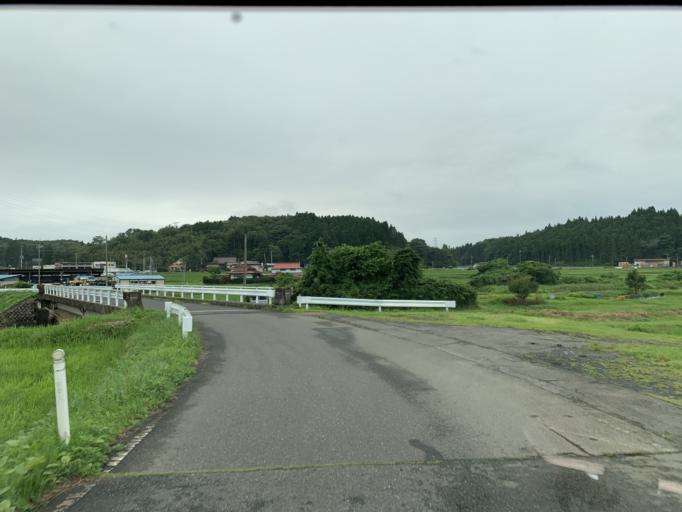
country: JP
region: Iwate
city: Ichinoseki
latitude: 38.8582
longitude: 141.1539
